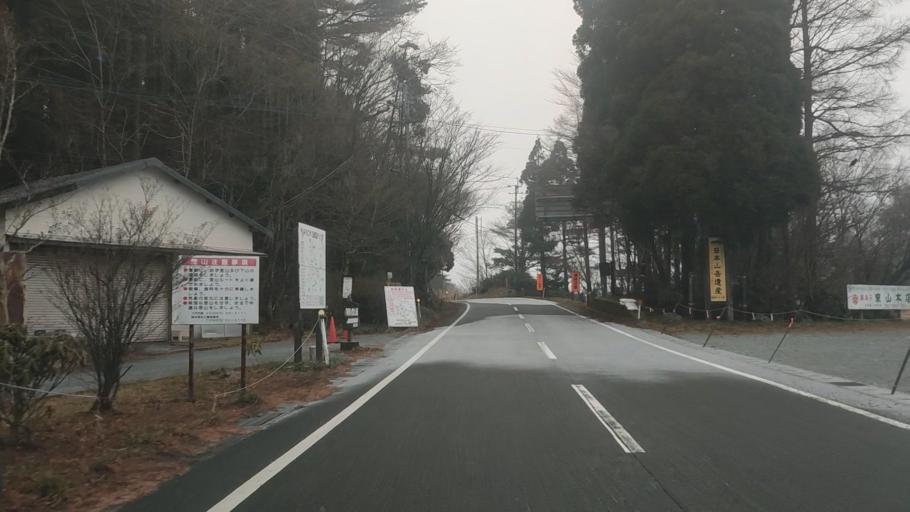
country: JP
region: Kumamoto
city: Matsubase
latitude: 32.5744
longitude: 130.9029
